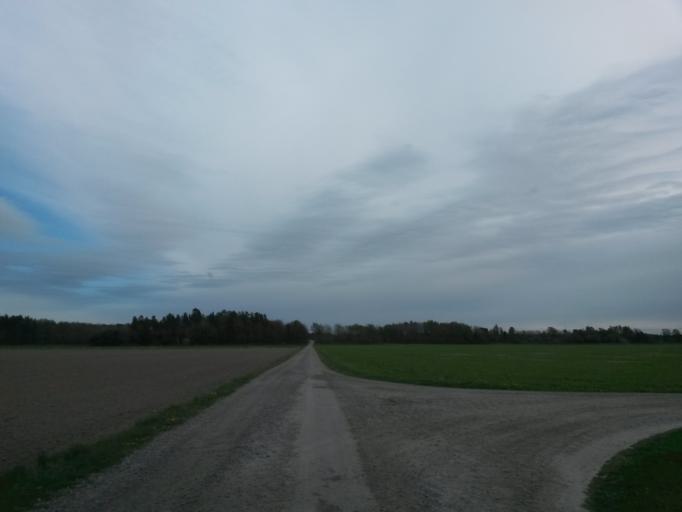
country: SE
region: Vaestra Goetaland
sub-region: Grastorps Kommun
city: Graestorp
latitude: 58.3743
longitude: 12.8236
